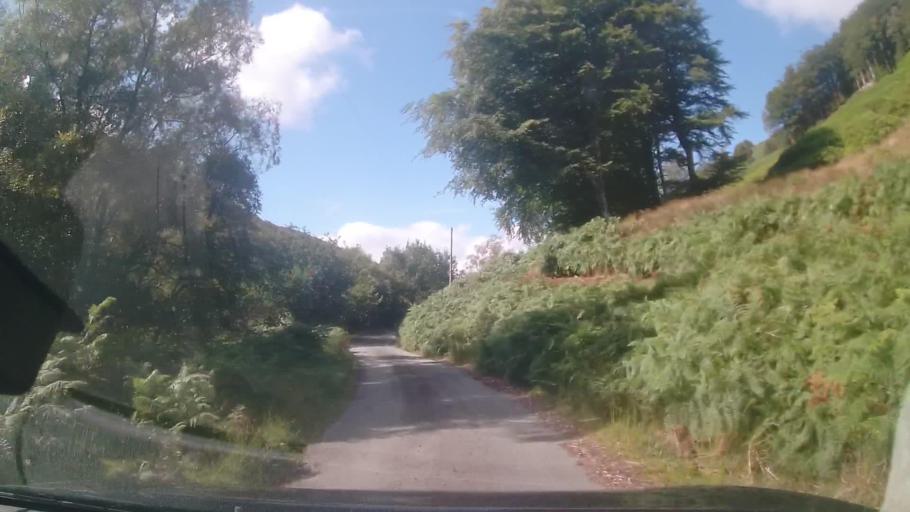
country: GB
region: Wales
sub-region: Gwynedd
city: Bala
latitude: 52.7916
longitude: -3.5516
